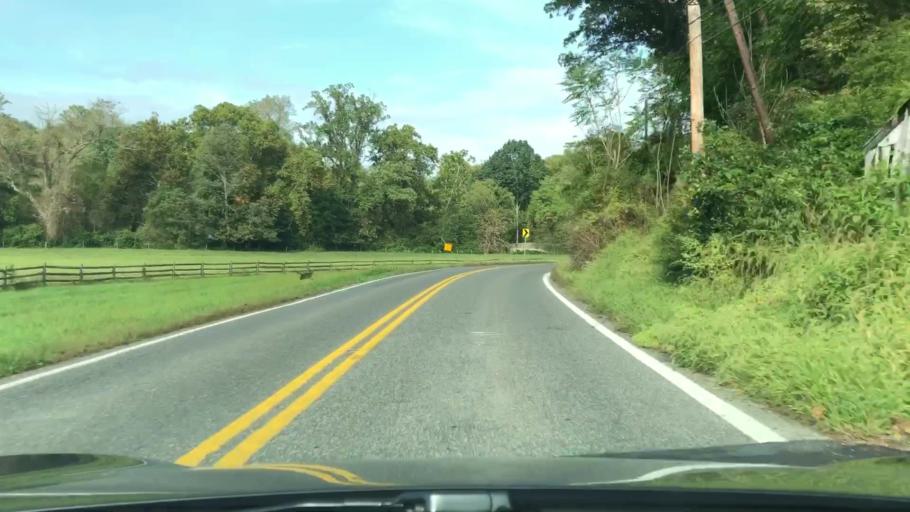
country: US
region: Pennsylvania
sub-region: Delaware County
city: Wayne
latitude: 40.0115
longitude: -75.3852
